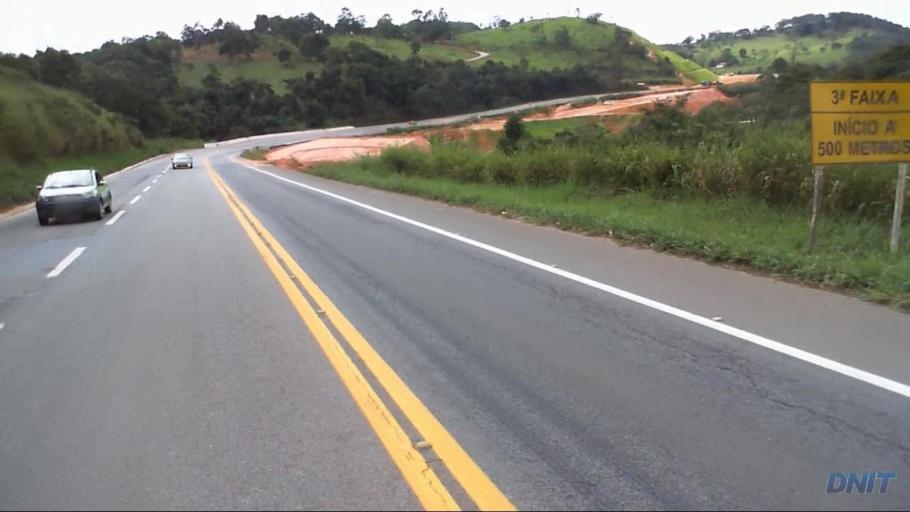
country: BR
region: Minas Gerais
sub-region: Caete
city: Caete
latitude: -19.7487
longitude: -43.6250
